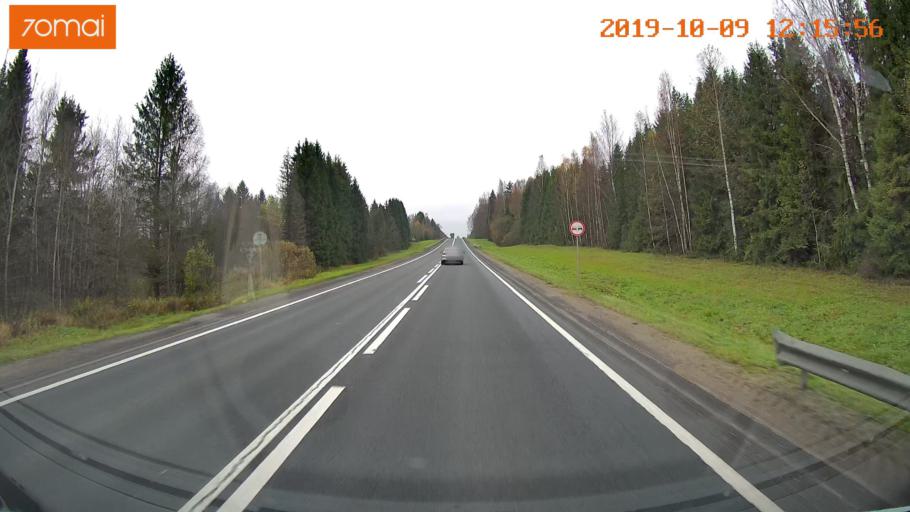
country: RU
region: Jaroslavl
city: Prechistoye
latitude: 58.4759
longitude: 40.3220
